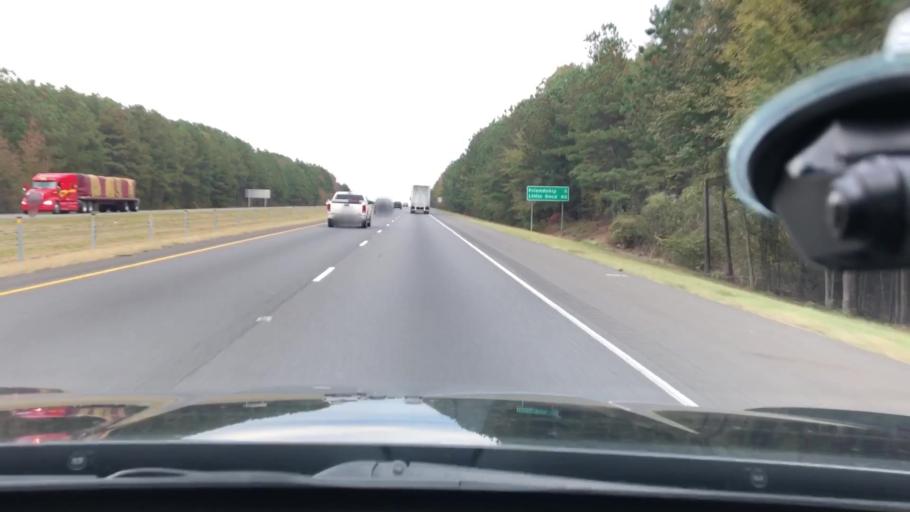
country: US
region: Arkansas
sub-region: Clark County
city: Arkadelphia
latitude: 34.1924
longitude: -93.0608
